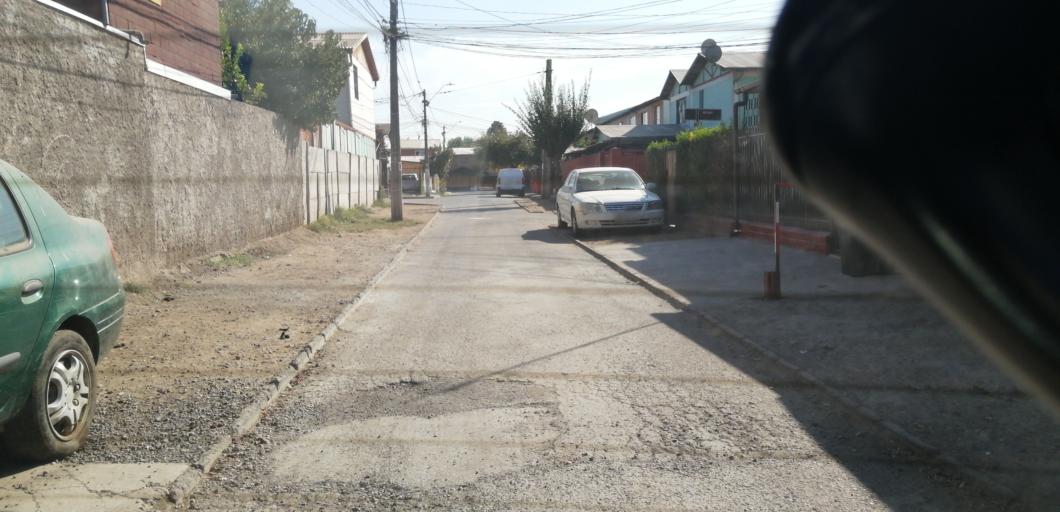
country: CL
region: Santiago Metropolitan
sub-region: Provincia de Santiago
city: Lo Prado
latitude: -33.4606
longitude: -70.7435
